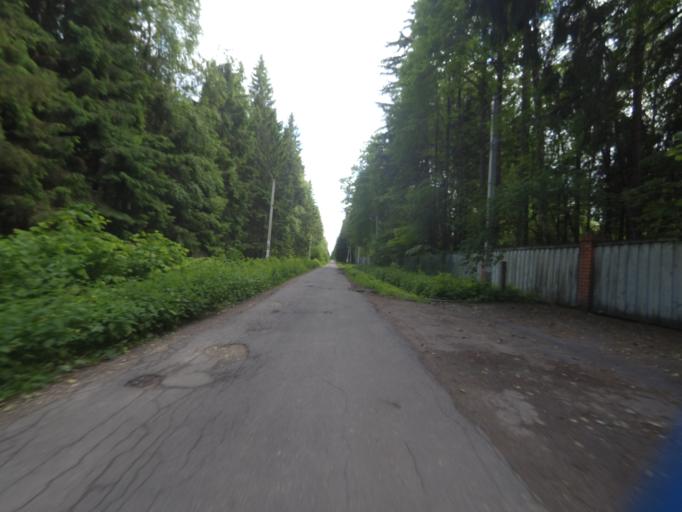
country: RU
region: Moskovskaya
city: Nekrasovskiy
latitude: 56.1193
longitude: 37.5173
